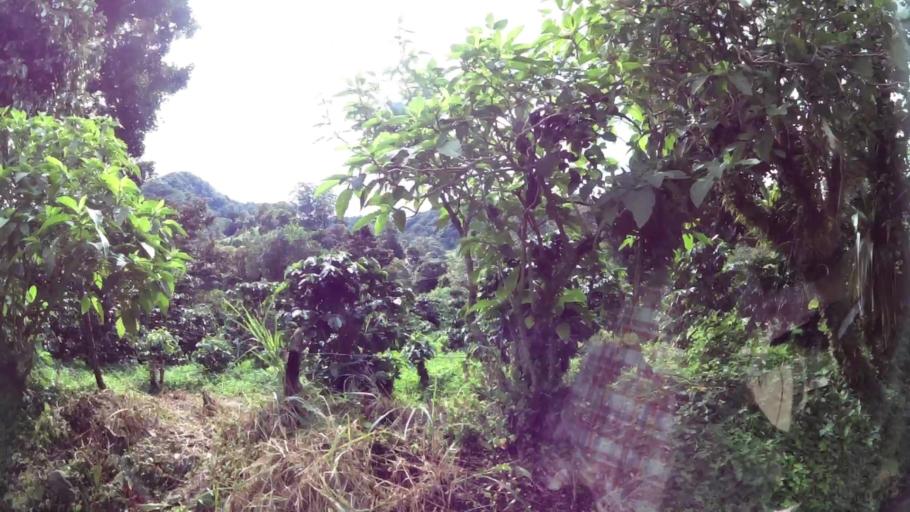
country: PA
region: Chiriqui
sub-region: Distrito Boquete
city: Boquete
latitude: 8.8022
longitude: -82.4235
